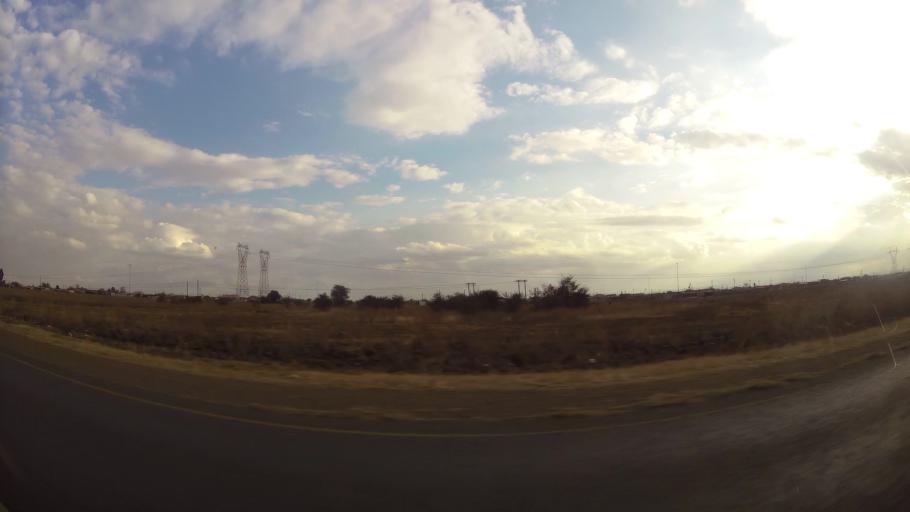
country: ZA
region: Gauteng
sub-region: Sedibeng District Municipality
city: Vanderbijlpark
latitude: -26.6831
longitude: 27.7976
